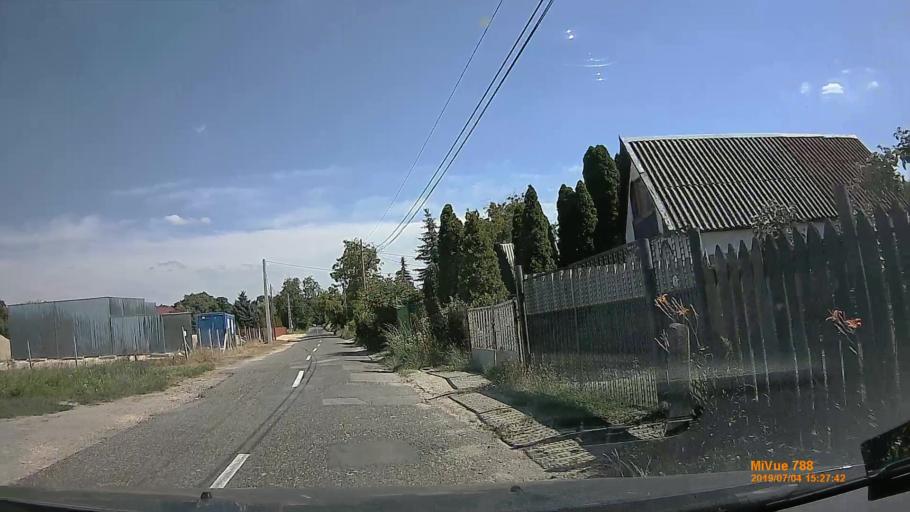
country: HU
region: Komarom-Esztergom
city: Tatabanya
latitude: 47.5415
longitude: 18.3841
